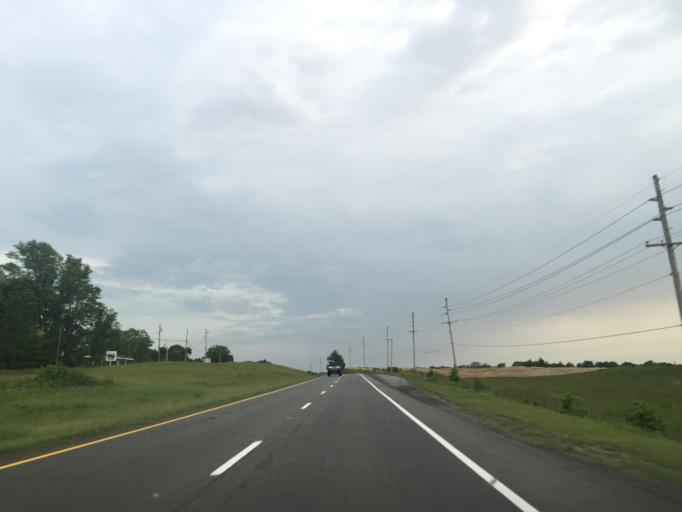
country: US
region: Virginia
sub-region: Clarke County
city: Berryville
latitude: 39.1735
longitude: -77.9709
